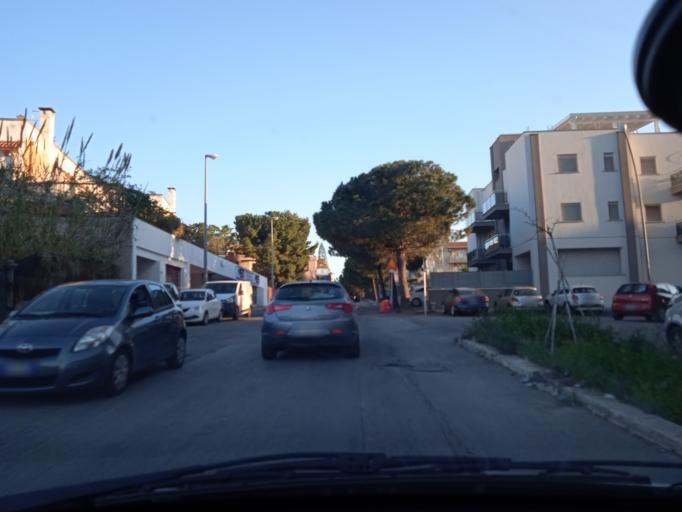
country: IT
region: Sicily
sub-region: Palermo
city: Bagheria
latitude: 38.0864
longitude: 13.5009
